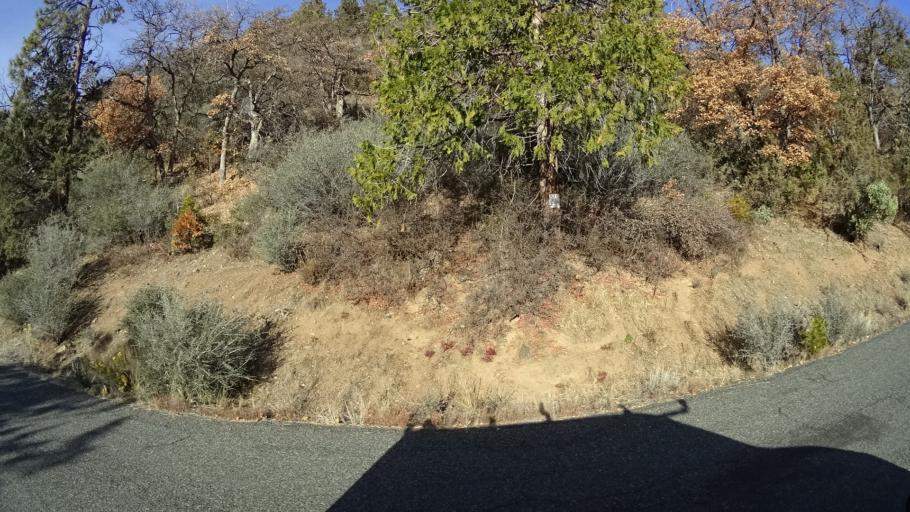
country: US
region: California
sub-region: Siskiyou County
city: Yreka
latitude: 41.6523
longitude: -122.6304
